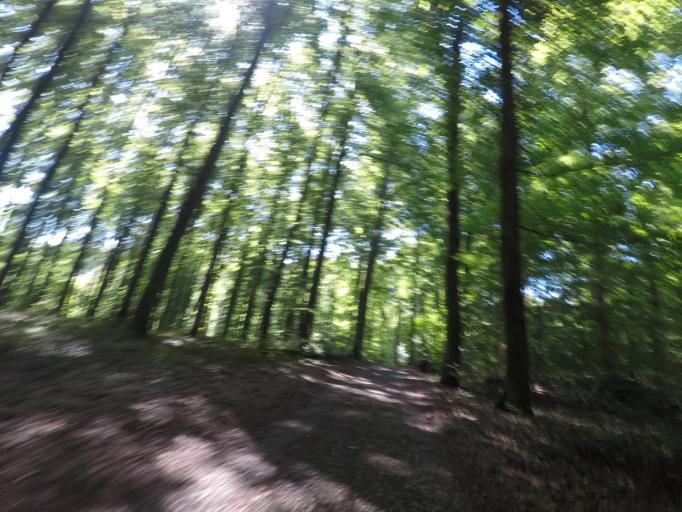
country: LU
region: Luxembourg
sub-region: Canton de Luxembourg
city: Strassen
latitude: 49.6367
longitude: 6.0731
